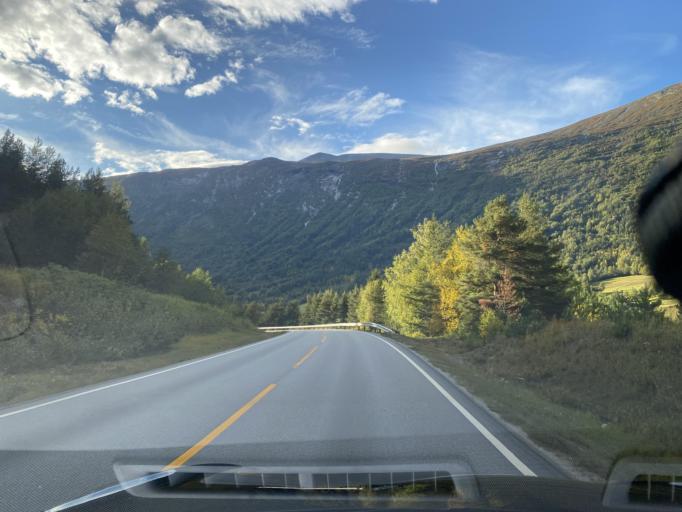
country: NO
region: Oppland
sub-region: Lom
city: Fossbergom
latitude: 61.8091
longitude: 8.4785
